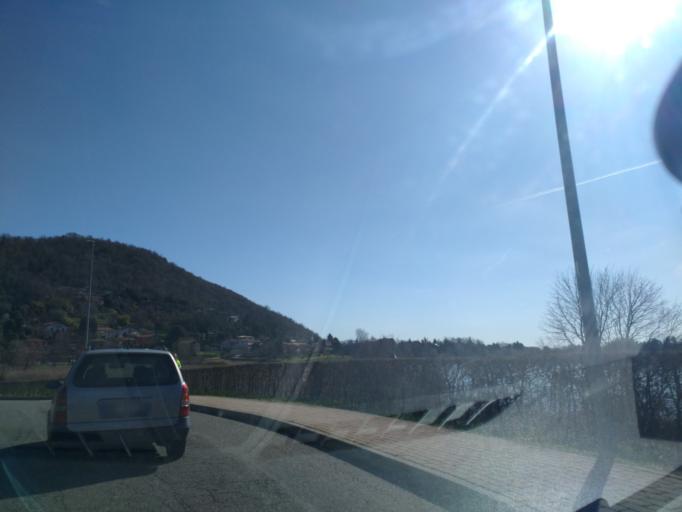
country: IT
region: Lombardy
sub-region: Provincia di Como
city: Montorfano
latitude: 45.7860
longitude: 9.1352
